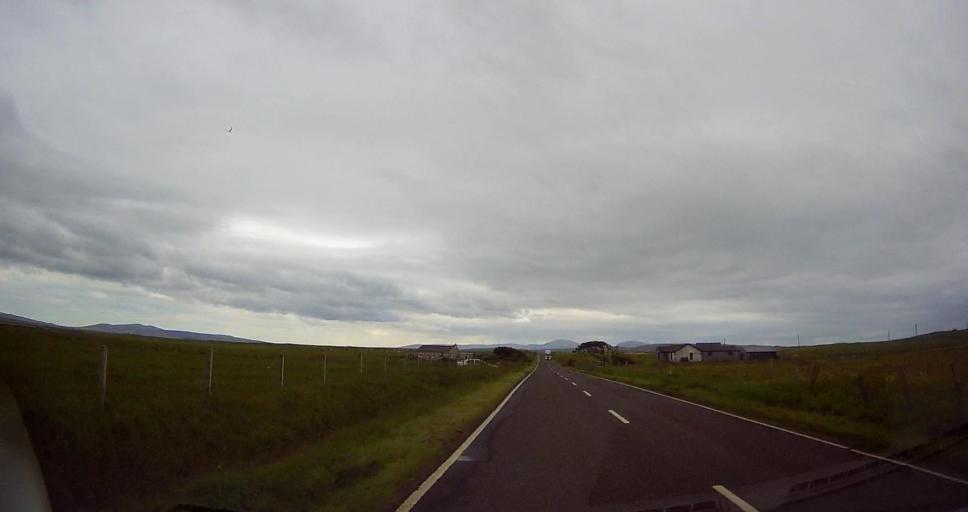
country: GB
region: Scotland
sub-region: Orkney Islands
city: Stromness
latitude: 59.0726
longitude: -3.2792
